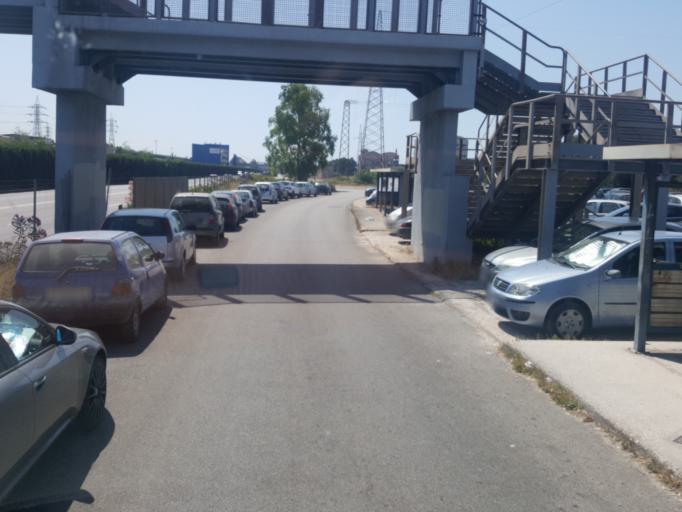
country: IT
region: Apulia
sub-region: Provincia di Taranto
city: Statte
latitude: 40.5043
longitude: 17.1974
